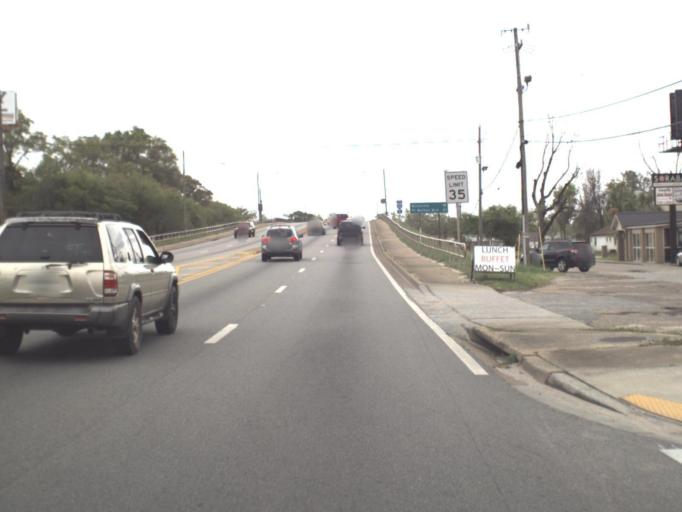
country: US
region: Florida
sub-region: Okaloosa County
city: Crestview
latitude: 30.7600
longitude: -86.5698
